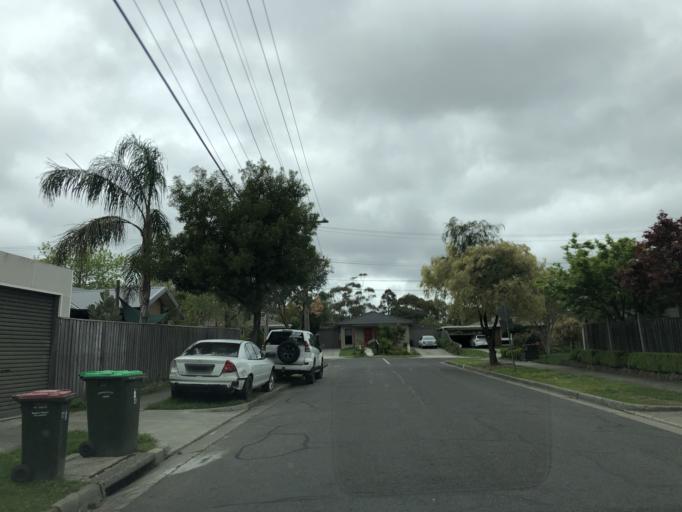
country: AU
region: Victoria
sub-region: Whitehorse
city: Forest Hill
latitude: -37.8402
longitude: 145.1636
